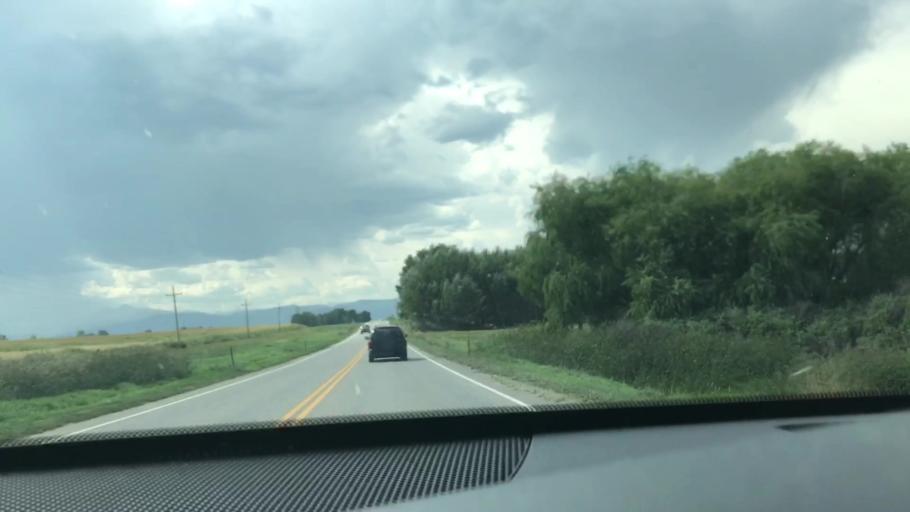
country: US
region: Colorado
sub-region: Larimer County
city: Loveland
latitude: 40.3793
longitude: -105.0058
